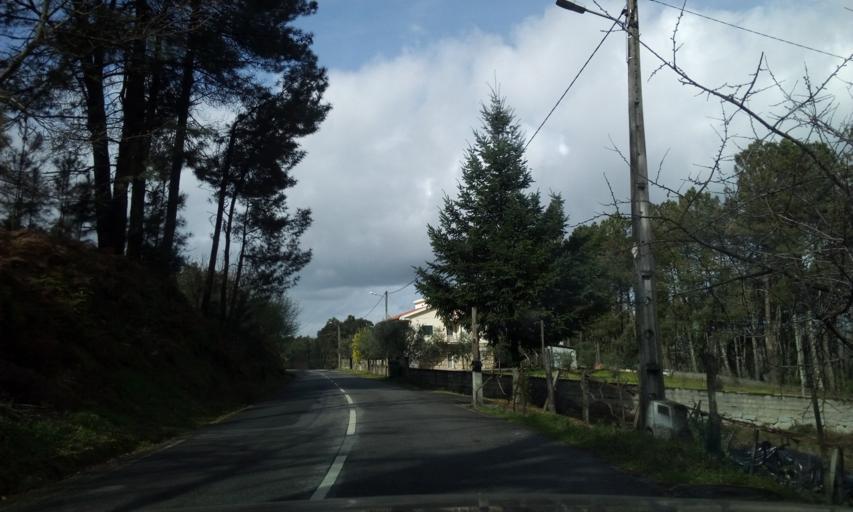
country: PT
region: Guarda
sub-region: Fornos de Algodres
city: Fornos de Algodres
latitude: 40.6602
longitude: -7.6332
